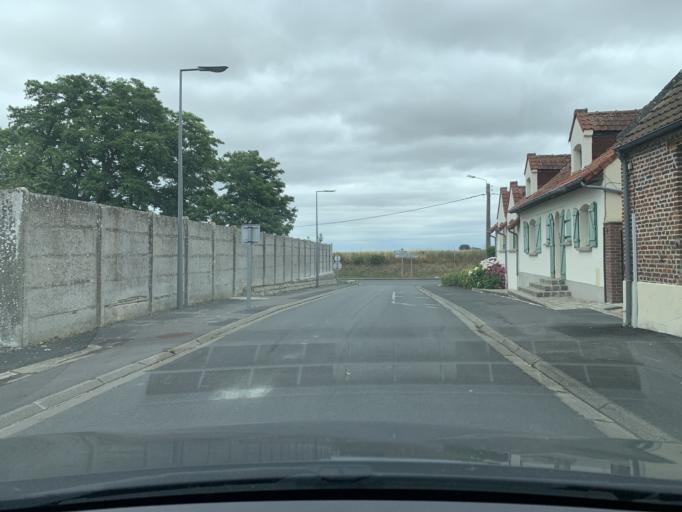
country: FR
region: Nord-Pas-de-Calais
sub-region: Departement du Nord
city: Neuville-Saint-Remy
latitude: 50.1989
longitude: 3.2211
